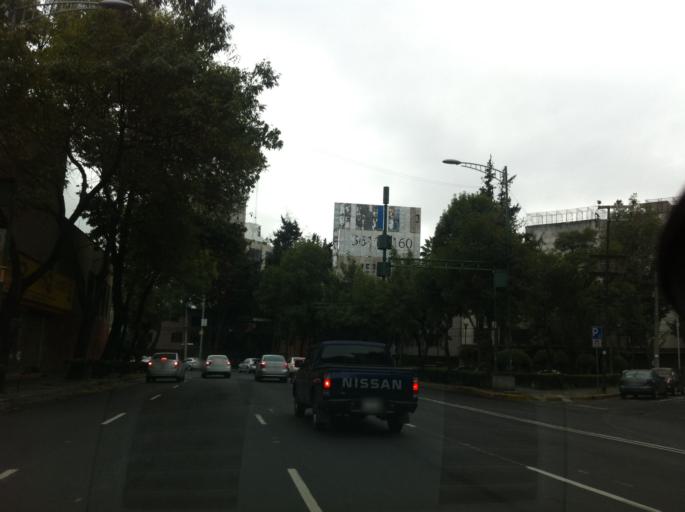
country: MX
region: Mexico City
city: Colonia del Valle
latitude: 19.3819
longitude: -99.1800
